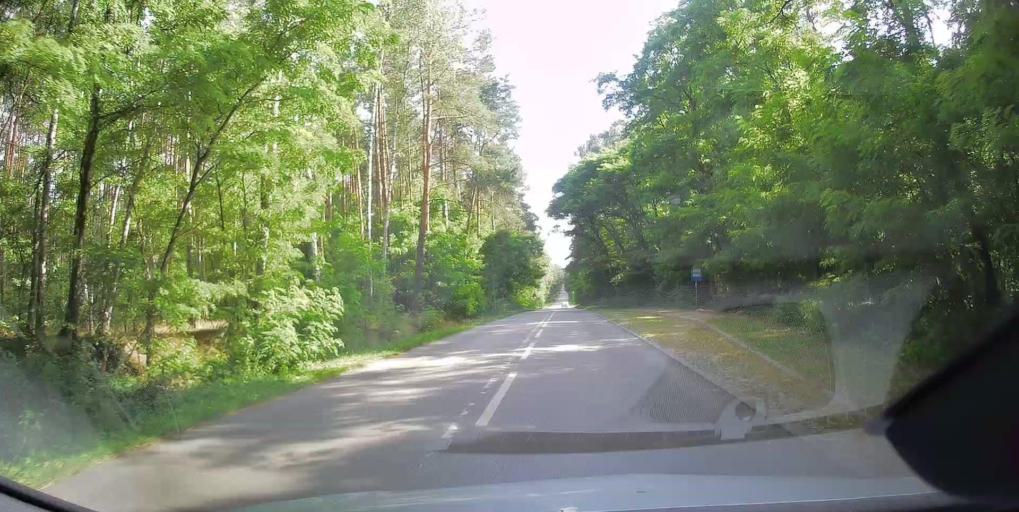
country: PL
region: Lodz Voivodeship
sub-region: Powiat opoczynski
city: Mniszkow
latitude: 51.3997
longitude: 20.0379
